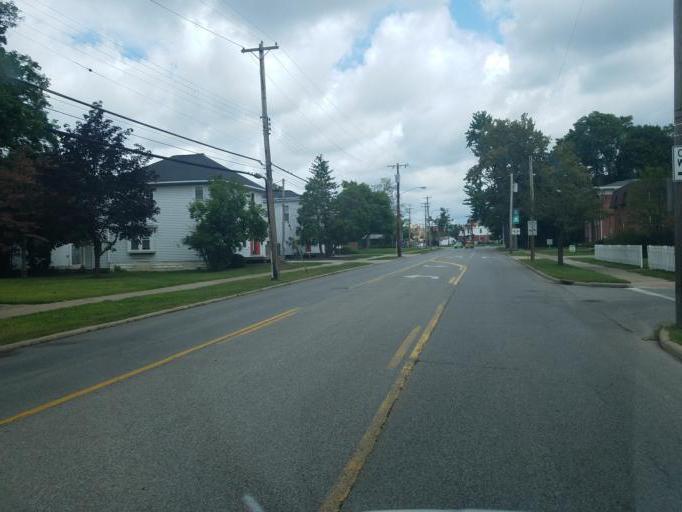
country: US
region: Ohio
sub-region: Lake County
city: Painesville
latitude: 41.7217
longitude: -81.2495
